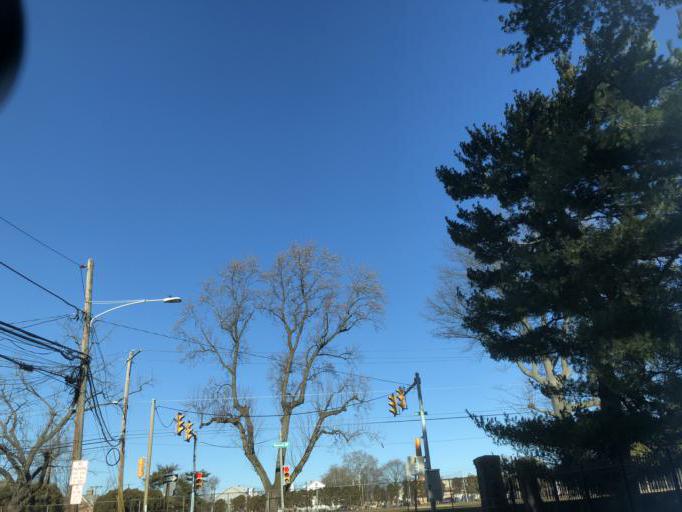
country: US
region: Pennsylvania
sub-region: Delaware County
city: Millbourne
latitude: 39.9562
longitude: -75.2555
